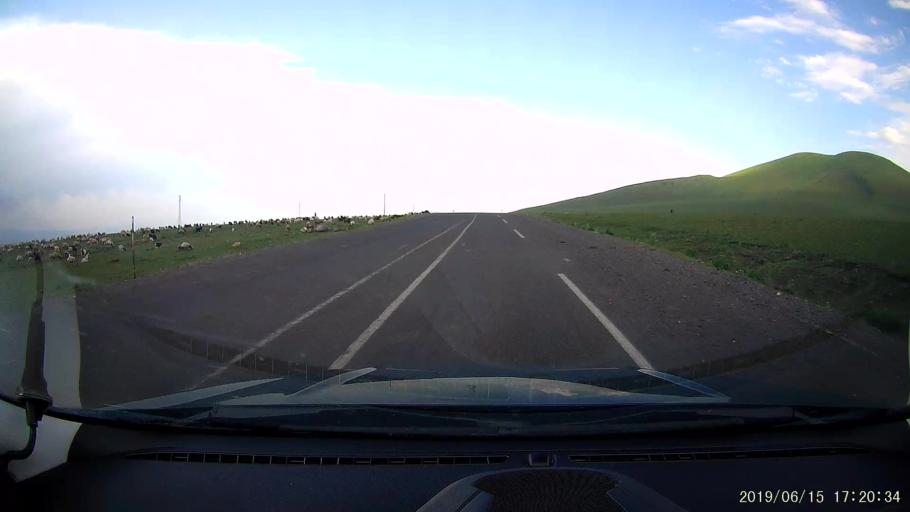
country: TR
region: Kars
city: Basgedikler
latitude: 40.6163
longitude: 43.3049
